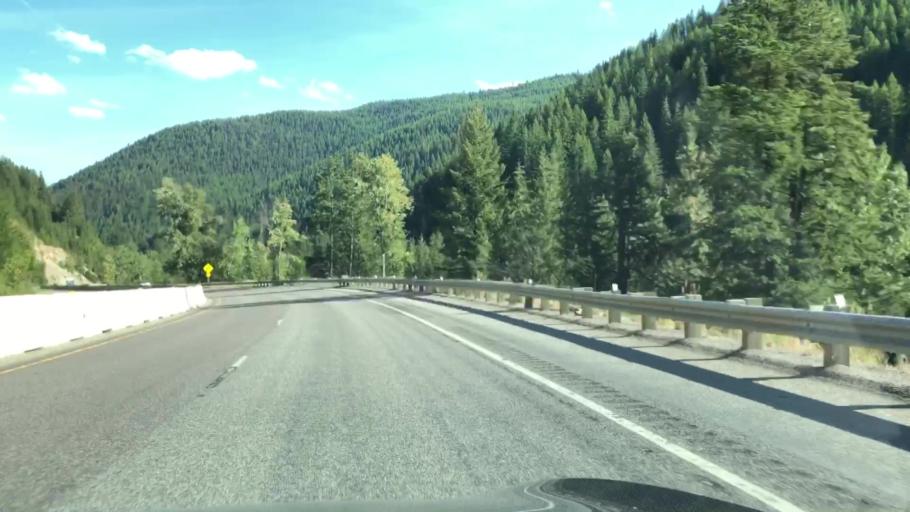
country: US
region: Montana
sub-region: Sanders County
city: Thompson Falls
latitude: 47.3996
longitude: -115.4611
